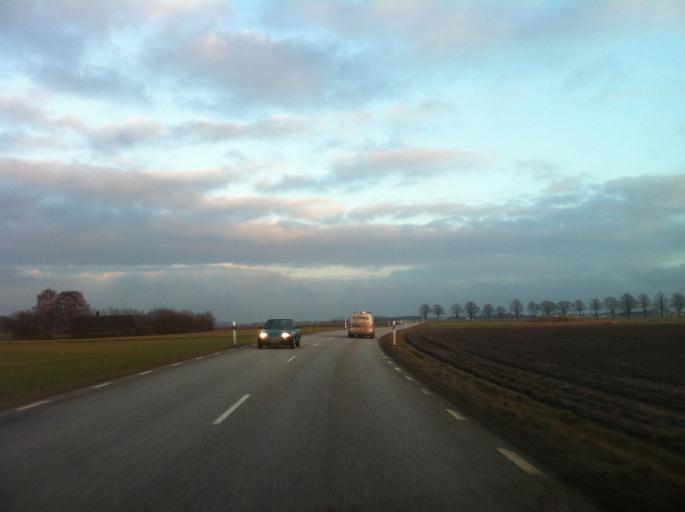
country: SE
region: Skane
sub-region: Kavlinge Kommun
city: Kaevlinge
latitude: 55.8058
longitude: 13.0758
